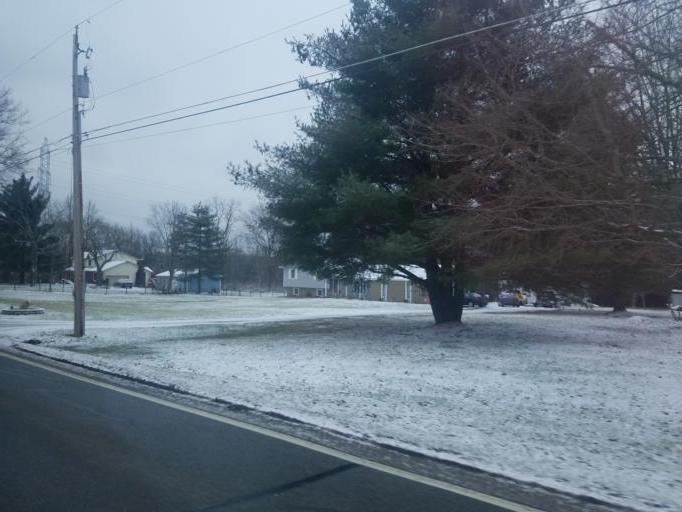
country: US
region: Ohio
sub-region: Franklin County
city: New Albany
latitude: 40.0411
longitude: -82.7878
